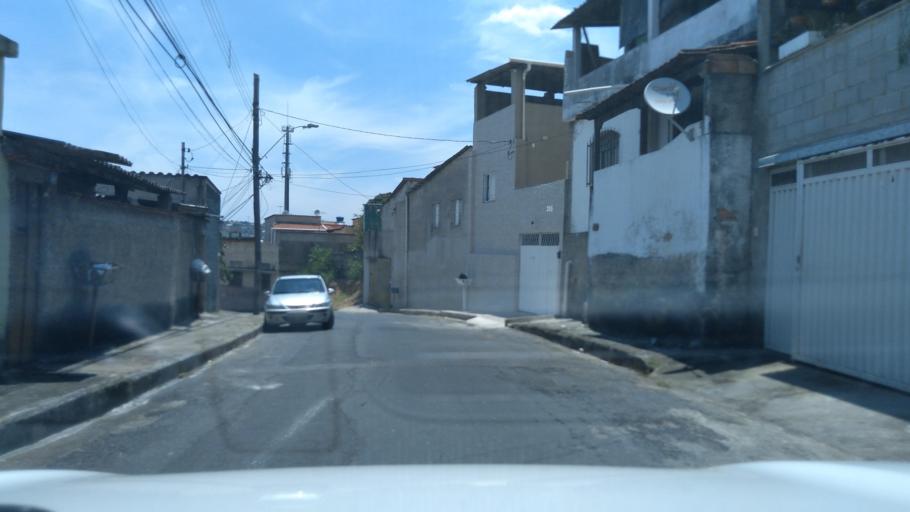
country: BR
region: Minas Gerais
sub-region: Contagem
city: Contagem
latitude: -19.9007
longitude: -44.0128
